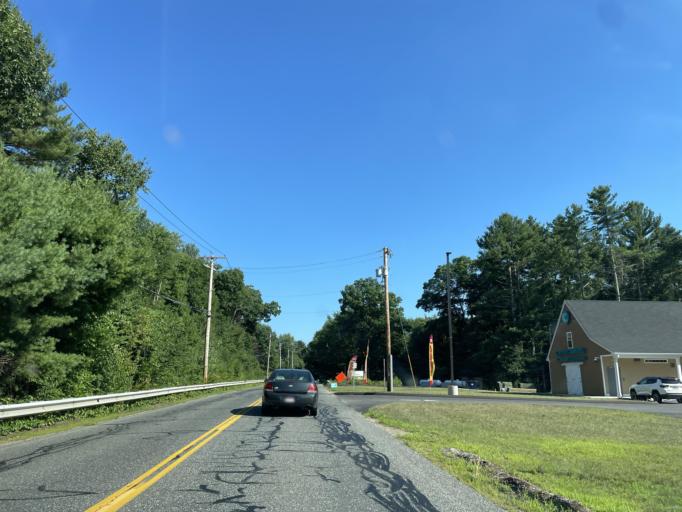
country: US
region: Massachusetts
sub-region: Worcester County
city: East Douglas
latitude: 42.0652
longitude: -71.6947
